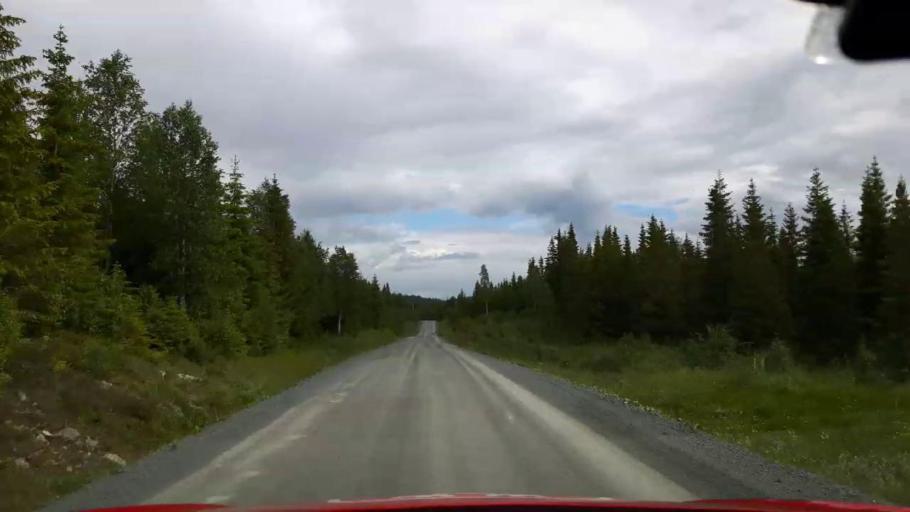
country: NO
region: Nord-Trondelag
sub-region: Lierne
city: Sandvika
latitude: 64.1446
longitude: 13.9228
